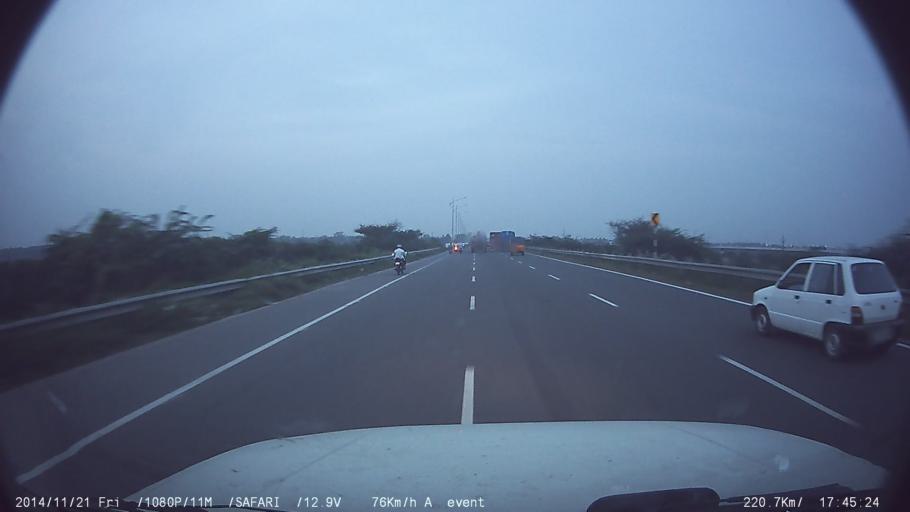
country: IN
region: Tamil Nadu
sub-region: Vellore
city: Arcot
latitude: 12.9134
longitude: 79.3247
